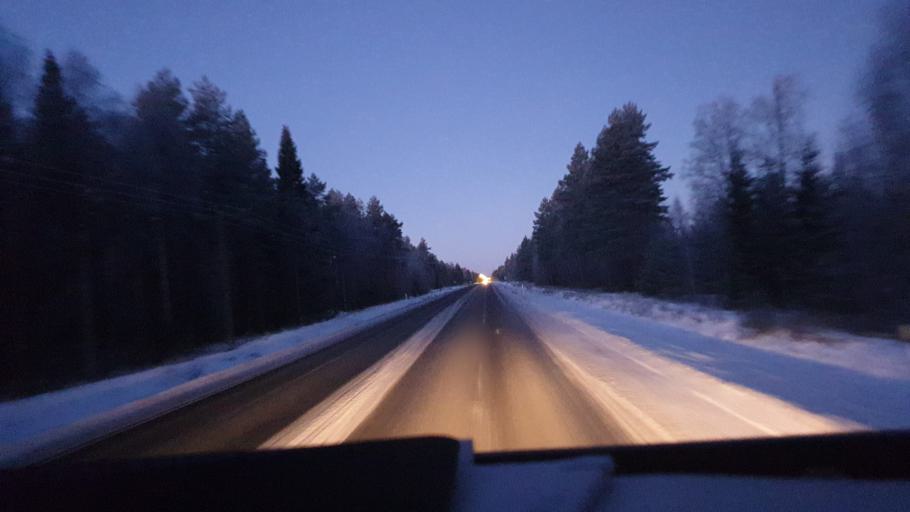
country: FI
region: Northern Ostrobothnia
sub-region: Raahe
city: Siikajoki
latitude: 64.6929
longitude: 24.6650
